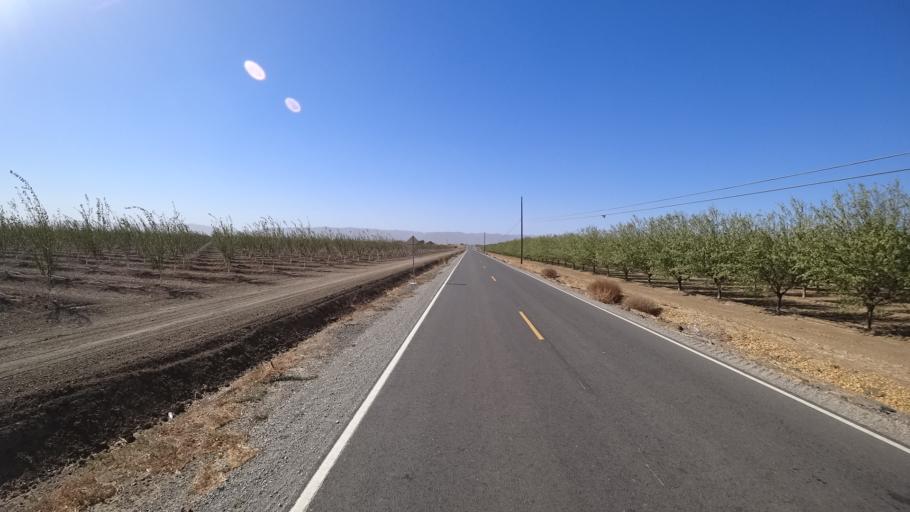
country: US
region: California
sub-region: Yolo County
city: Winters
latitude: 38.5840
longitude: -121.9454
